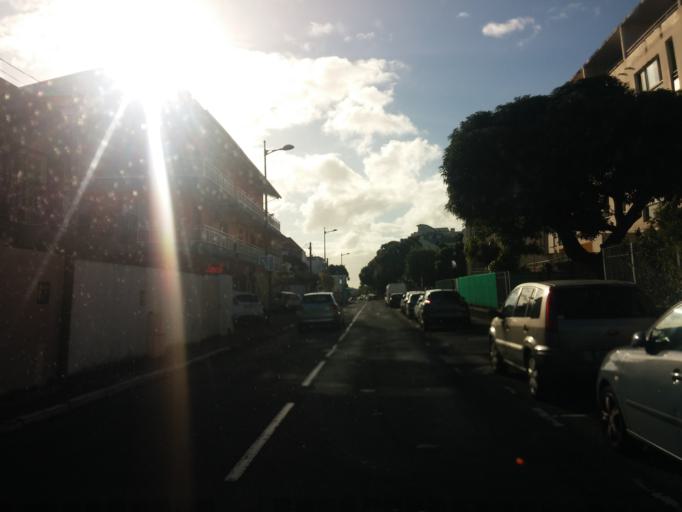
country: RE
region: Reunion
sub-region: Reunion
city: Saint-Denis
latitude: -20.8879
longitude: 55.4539
